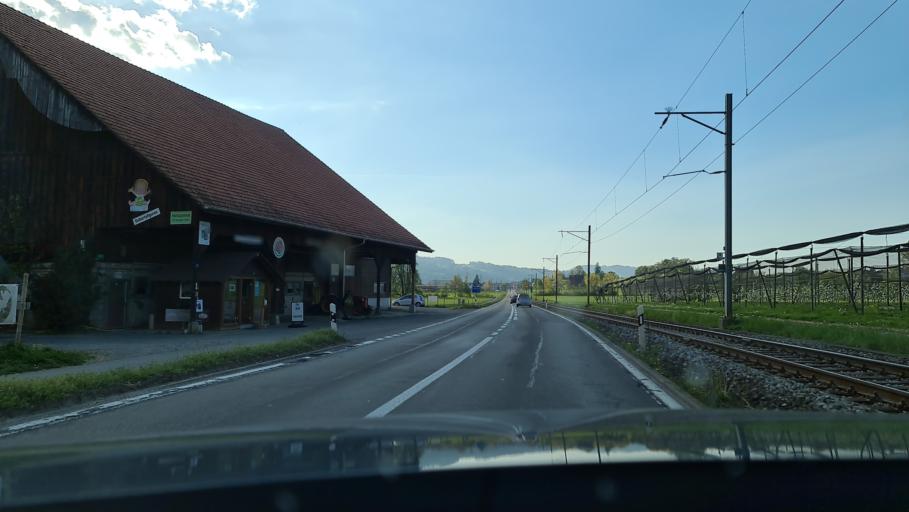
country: CH
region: Lucerne
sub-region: Hochdorf District
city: Hitzkirch
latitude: 47.2158
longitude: 8.2633
